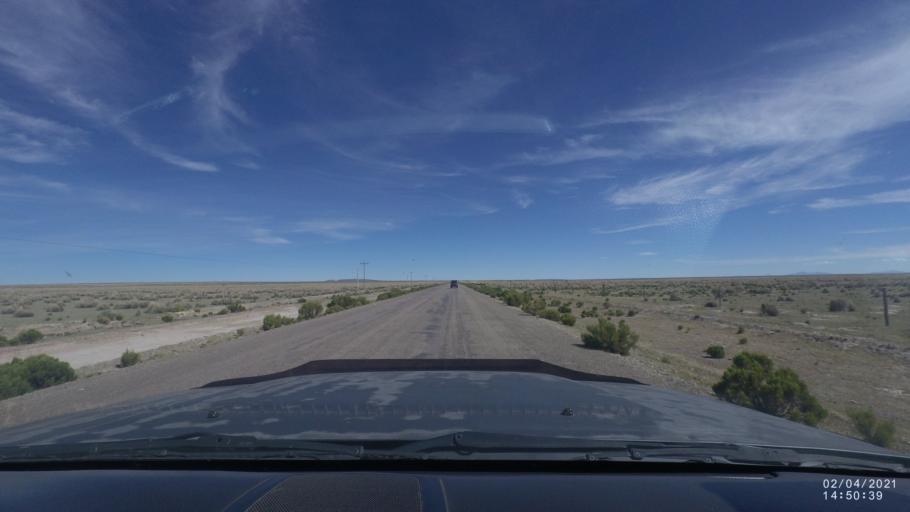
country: BO
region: Oruro
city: Poopo
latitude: -18.4407
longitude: -67.5944
